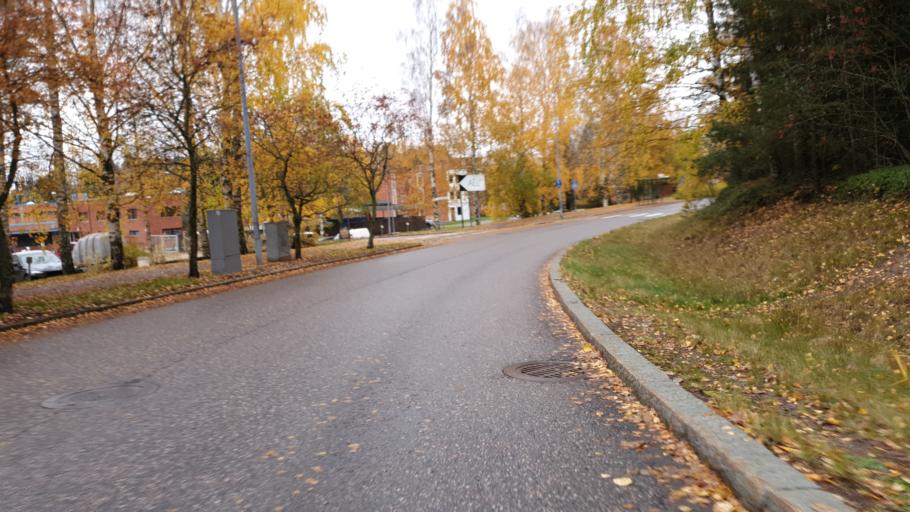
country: FI
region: Uusimaa
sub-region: Helsinki
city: Teekkarikylae
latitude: 60.2481
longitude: 24.8542
